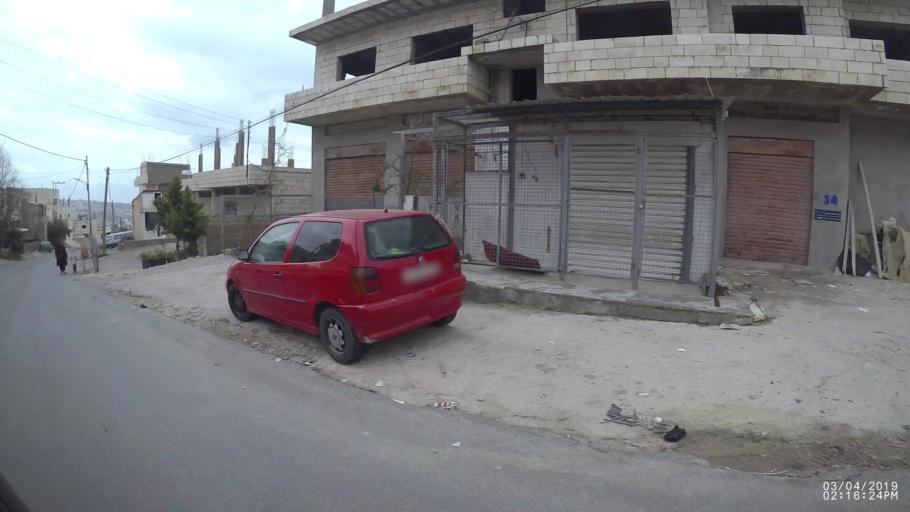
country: JO
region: Amman
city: Wadi as Sir
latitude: 31.9426
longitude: 35.8300
